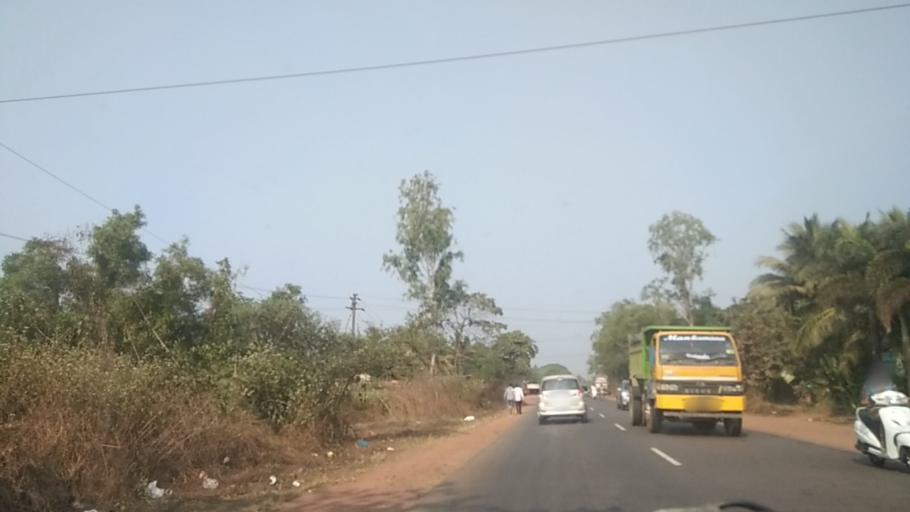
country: IN
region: Goa
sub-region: North Goa
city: Colovale
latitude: 15.6304
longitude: 73.8270
